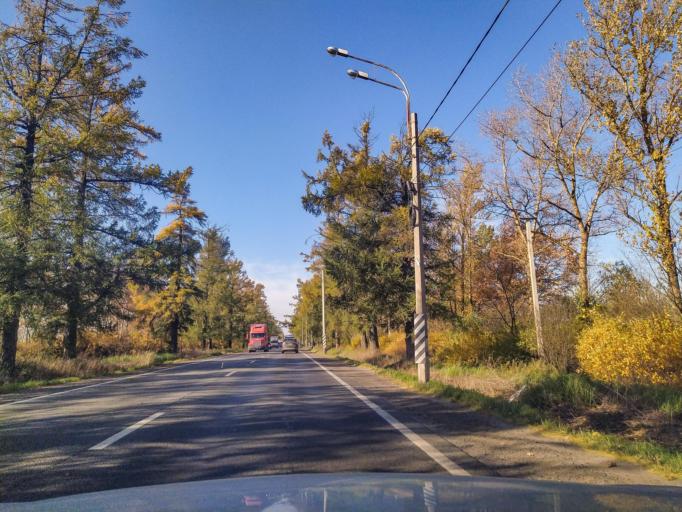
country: RU
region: St.-Petersburg
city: Aleksandrovskaya
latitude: 59.7061
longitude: 30.3383
